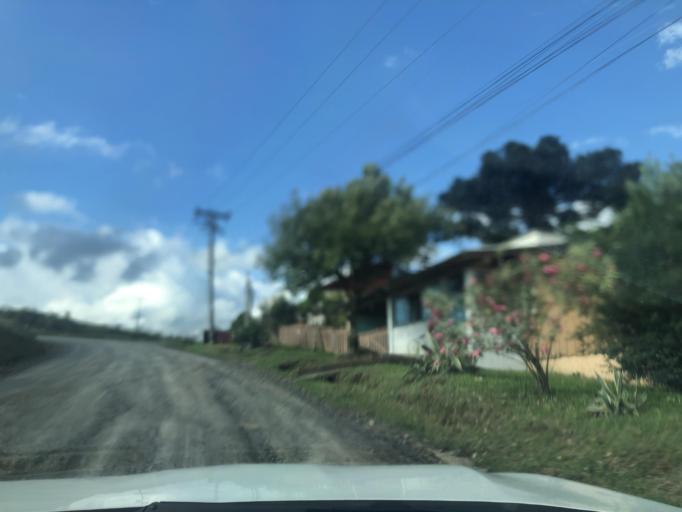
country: BR
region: Santa Catarina
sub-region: Lages
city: Lages
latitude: -27.7928
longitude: -50.3167
